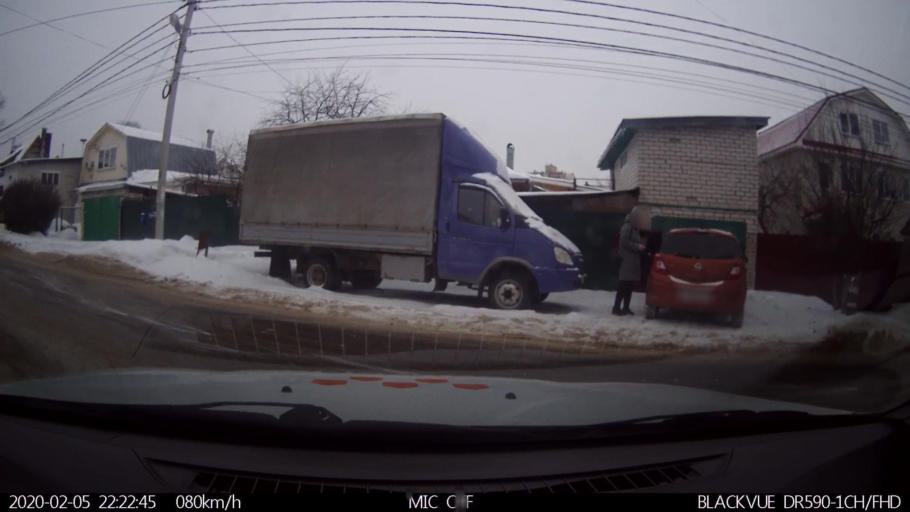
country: RU
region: Nizjnij Novgorod
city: Pervomaysk
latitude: 54.7649
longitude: 44.0180
